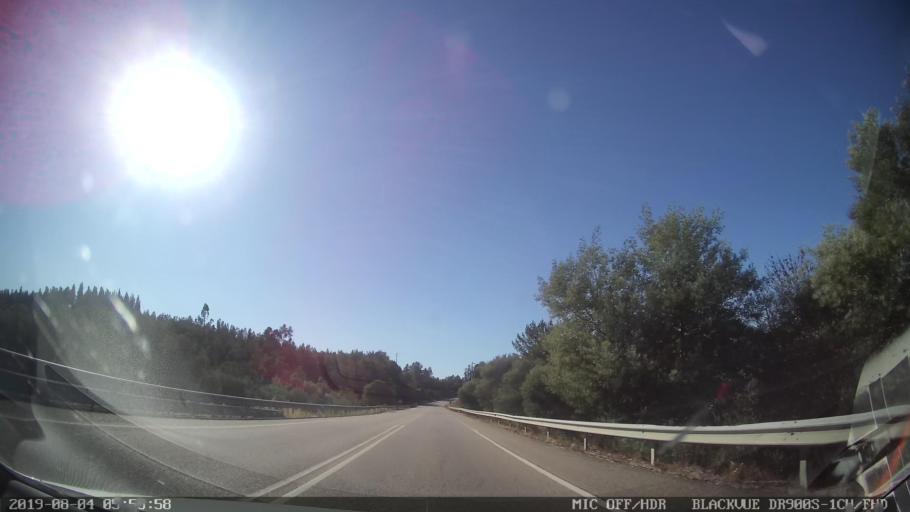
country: PT
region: Portalegre
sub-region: Gaviao
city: Gaviao
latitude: 39.4590
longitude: -7.9378
